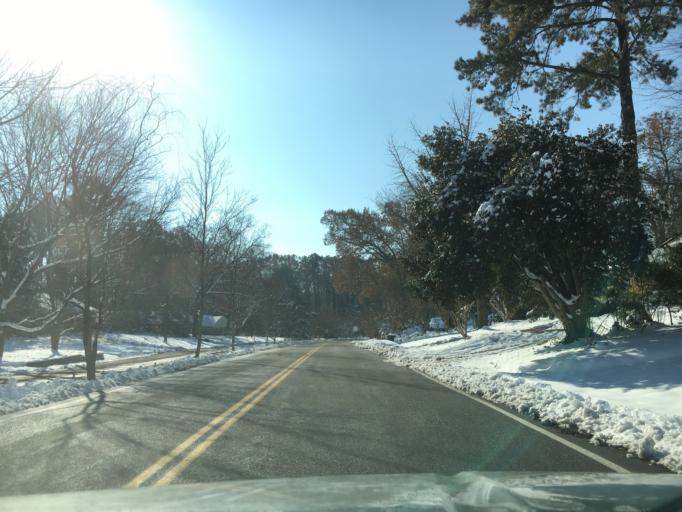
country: US
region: Virginia
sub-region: Henrico County
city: Tuckahoe
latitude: 37.5907
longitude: -77.5398
